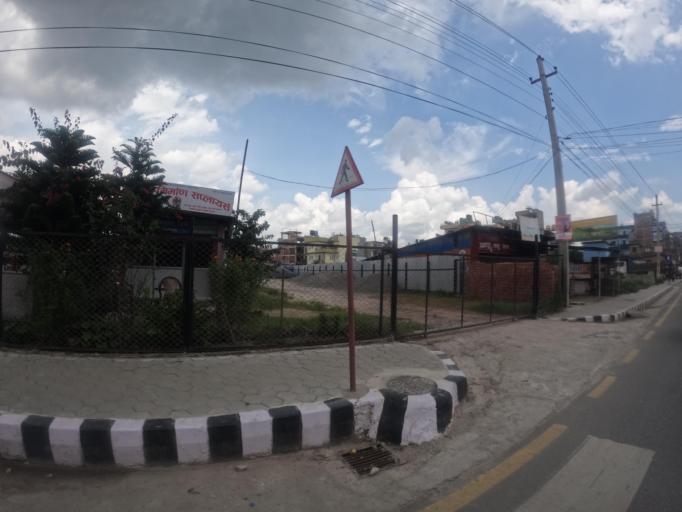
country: NP
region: Central Region
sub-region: Bagmati Zone
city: Bhaktapur
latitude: 27.6796
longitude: 85.4004
